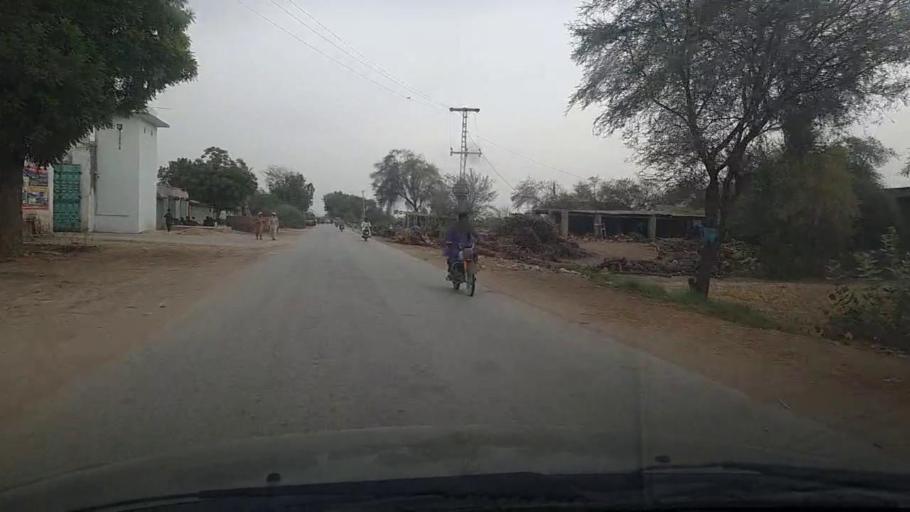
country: PK
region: Sindh
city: Daulatpur
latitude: 26.3124
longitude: 68.1013
